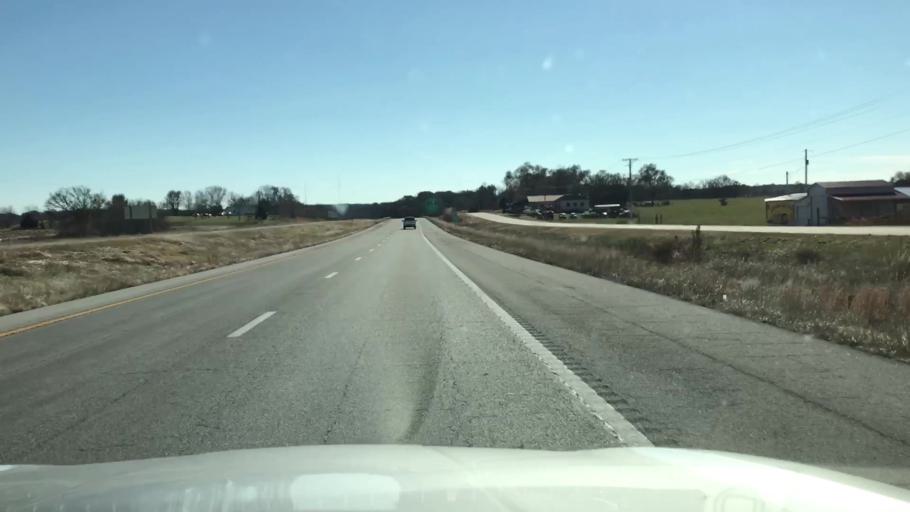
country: US
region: Missouri
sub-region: Jasper County
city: Carthage
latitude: 37.1197
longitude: -94.3113
